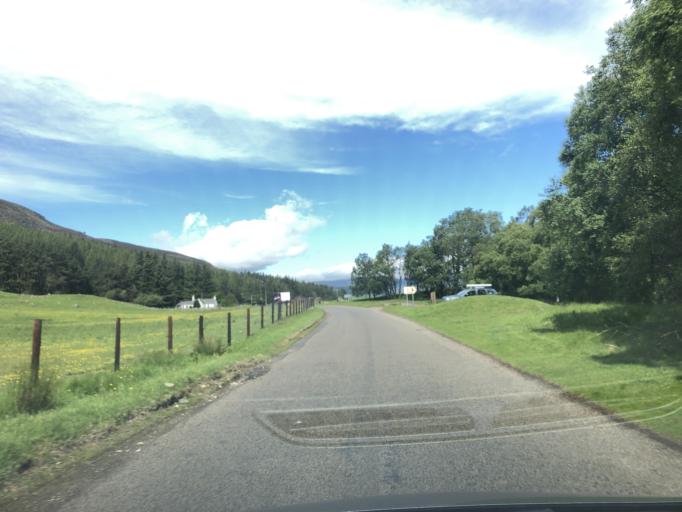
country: GB
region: Scotland
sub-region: Angus
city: Kirriemuir
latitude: 56.7727
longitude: -3.0277
